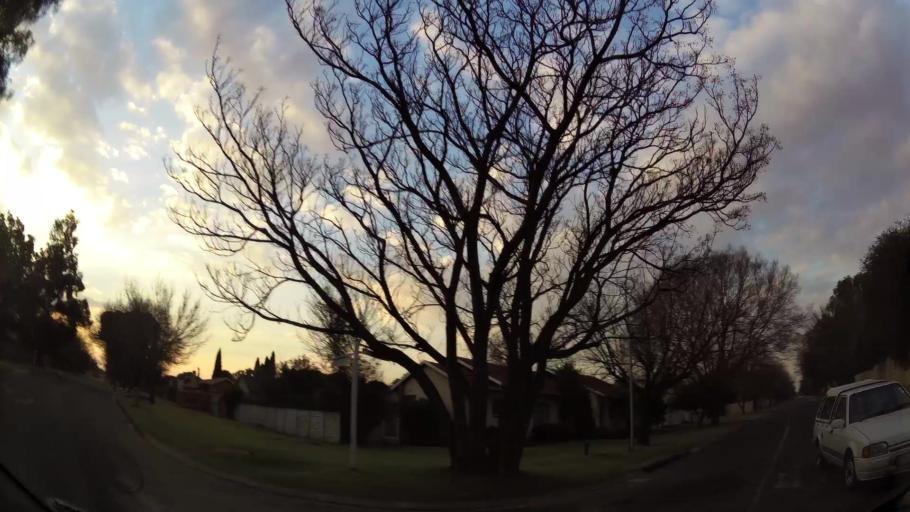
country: ZA
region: Gauteng
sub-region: Ekurhuleni Metropolitan Municipality
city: Benoni
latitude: -26.1702
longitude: 28.3036
